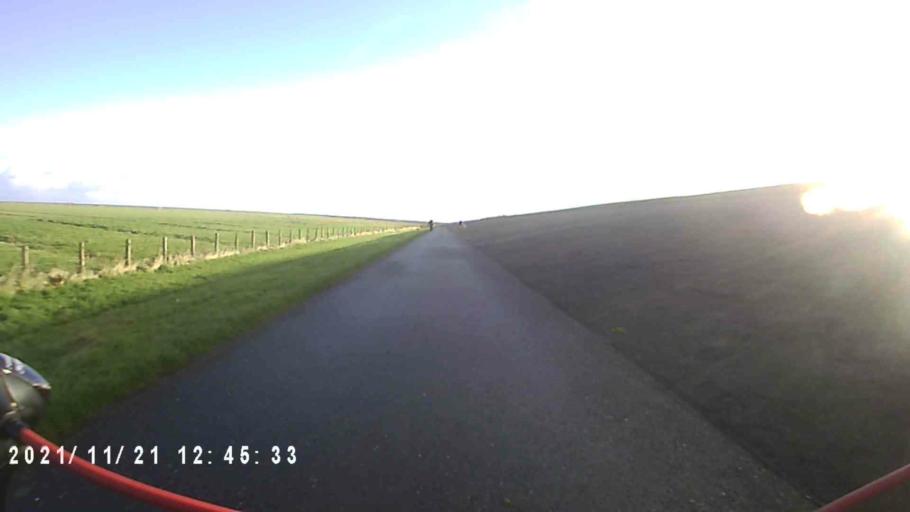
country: NL
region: Friesland
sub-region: Gemeente Dongeradeel
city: Anjum
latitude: 53.4009
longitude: 6.1065
